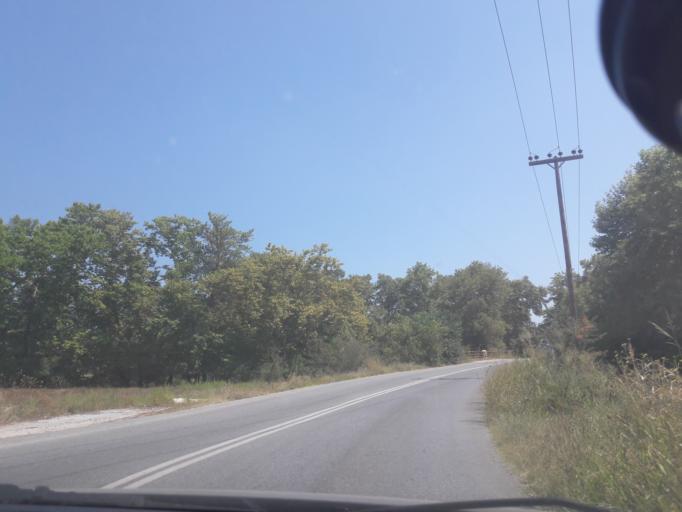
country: GR
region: Central Macedonia
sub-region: Nomos Chalkidikis
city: Megali Panagia
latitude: 40.3703
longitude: 23.6890
